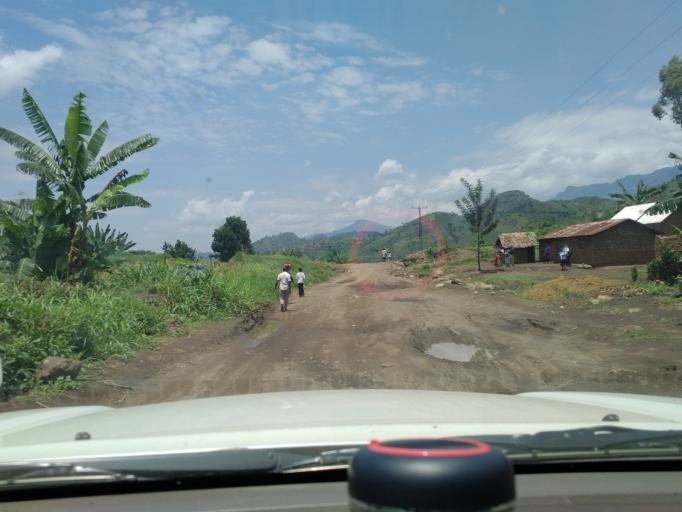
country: CD
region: Nord Kivu
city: Sake
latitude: -1.6585
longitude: 29.0234
